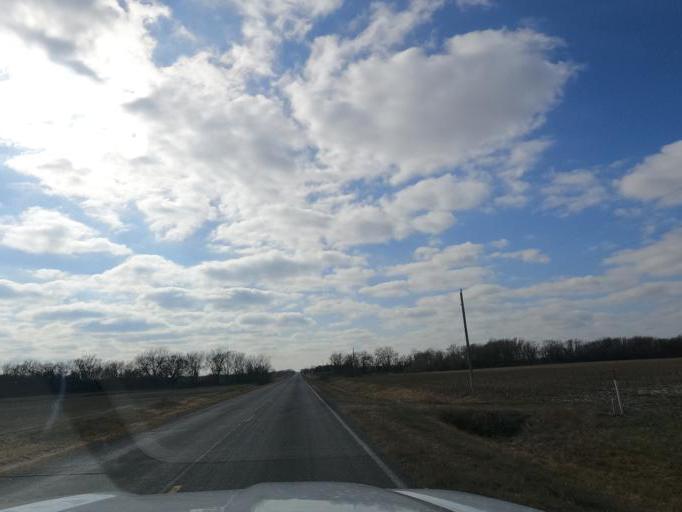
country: US
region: Kansas
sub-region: McPherson County
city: Inman
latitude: 38.2320
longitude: -97.8599
